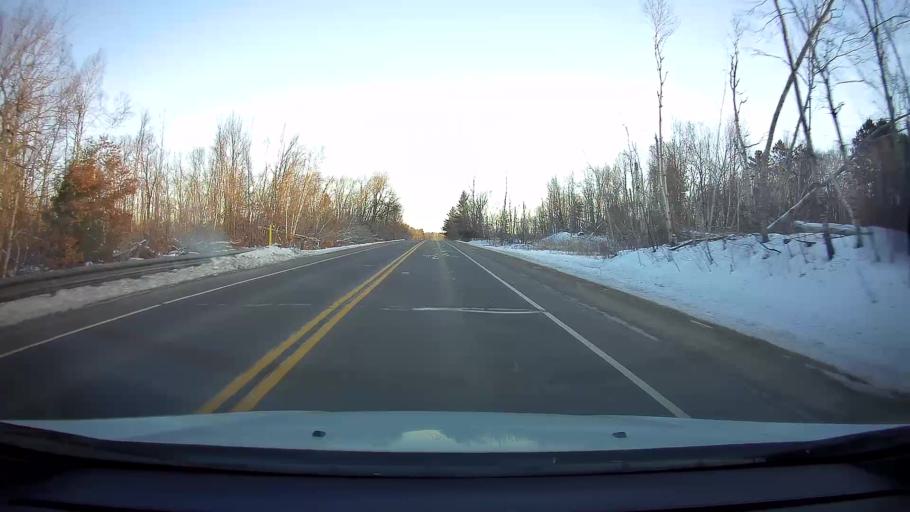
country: US
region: Wisconsin
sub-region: Barron County
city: Turtle Lake
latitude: 45.4214
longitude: -92.1303
